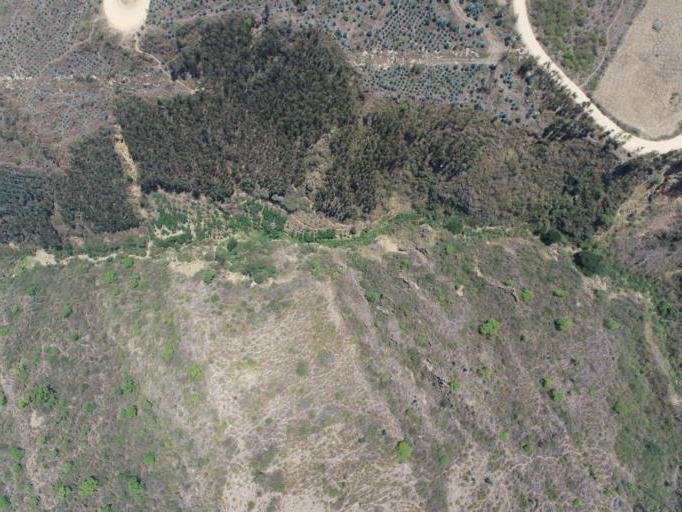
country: BO
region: La Paz
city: Quime
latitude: -16.9027
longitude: -67.1409
